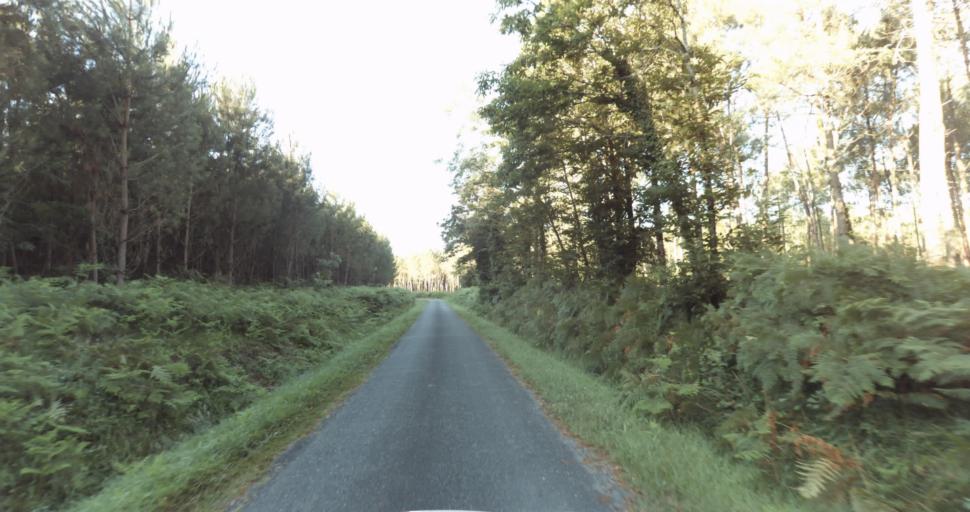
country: FR
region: Aquitaine
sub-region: Departement de la Gironde
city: Bazas
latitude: 44.4149
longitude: -0.2337
